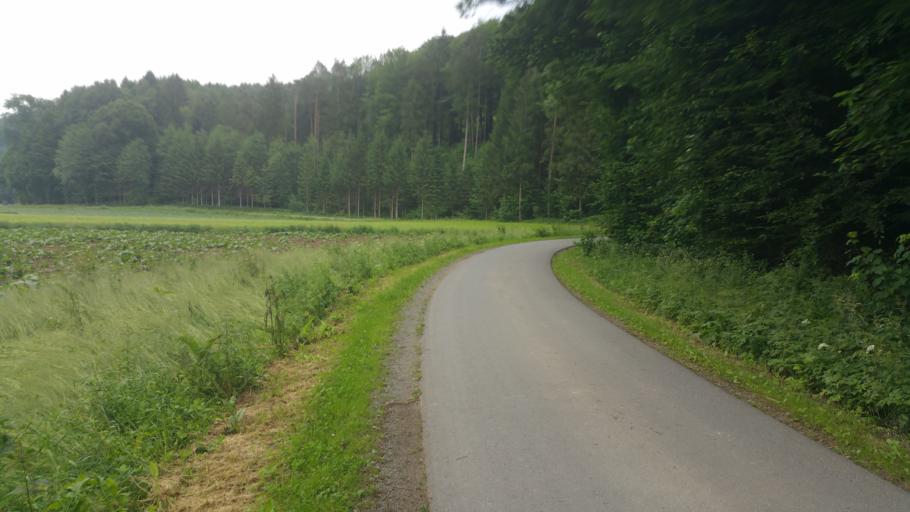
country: AT
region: Styria
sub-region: Politischer Bezirk Deutschlandsberg
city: Sankt Martin im Sulmtal
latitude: 46.7342
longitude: 15.3309
